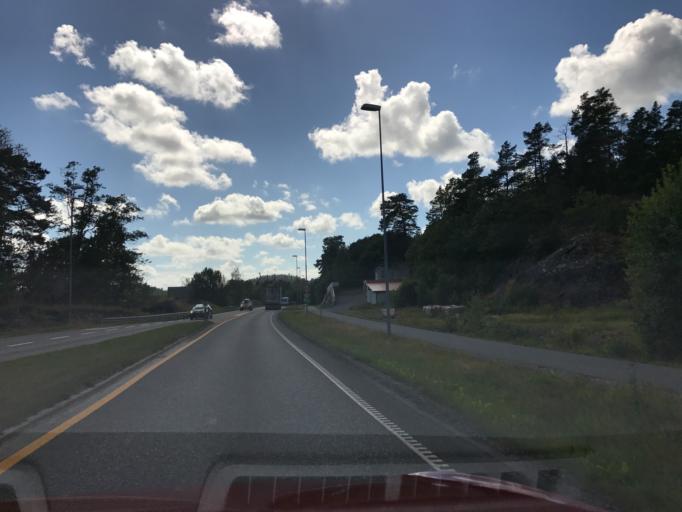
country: NO
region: Telemark
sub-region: Bamble
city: Langesund
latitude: 59.0145
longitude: 9.6728
